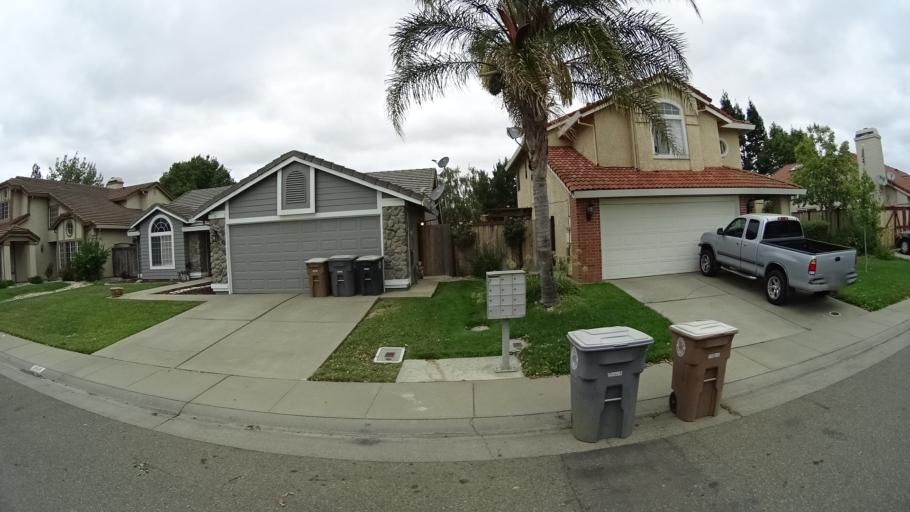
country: US
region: California
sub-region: Sacramento County
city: Laguna
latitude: 38.4188
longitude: -121.4509
